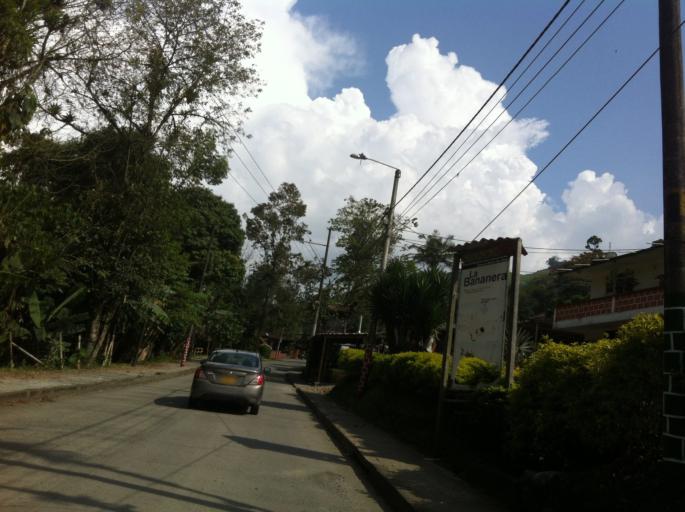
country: CO
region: Risaralda
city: Dos Quebradas
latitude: 4.7739
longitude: -75.6346
